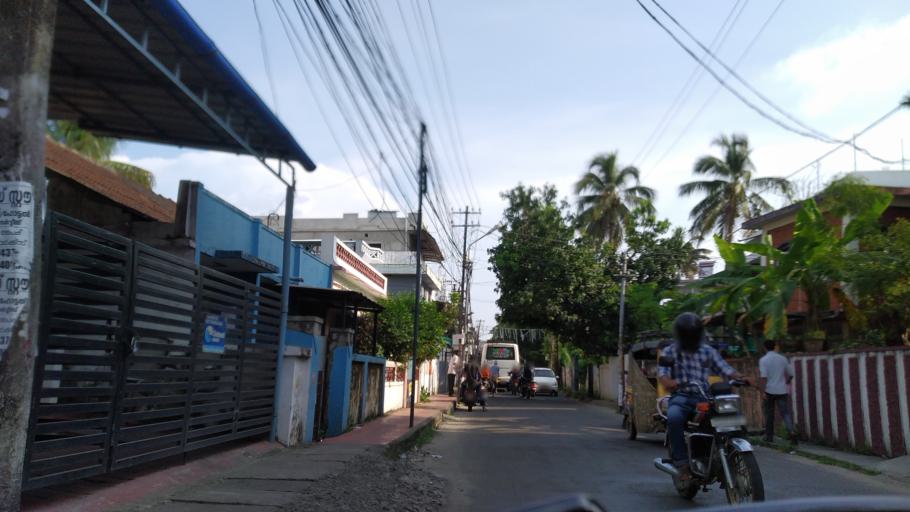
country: IN
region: Kerala
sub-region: Ernakulam
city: Cochin
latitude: 9.9997
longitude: 76.2843
